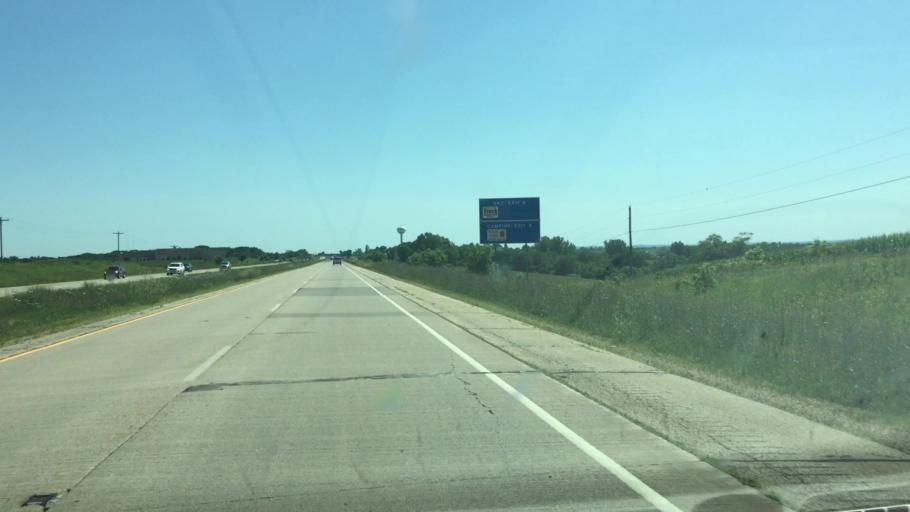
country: US
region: Wisconsin
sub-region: Grant County
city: Dickeyville
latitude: 42.5979
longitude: -90.5974
